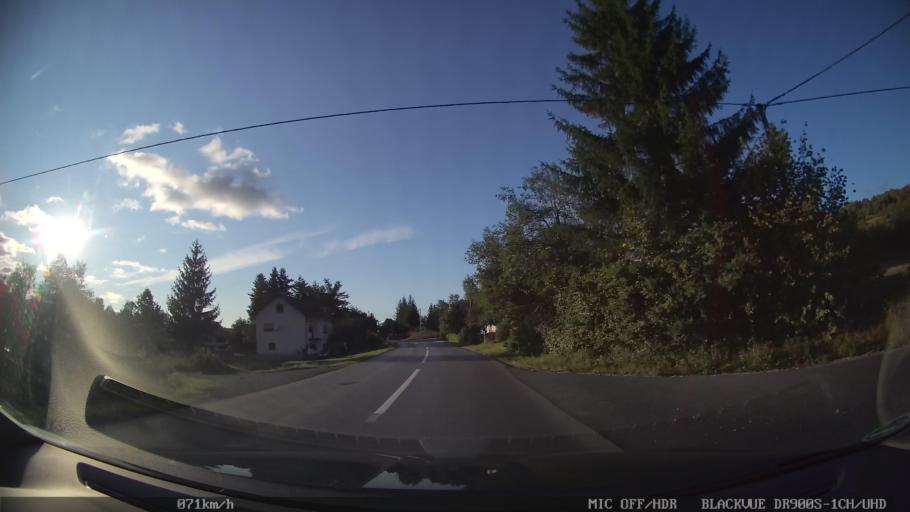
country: HR
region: Karlovacka
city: Plaski
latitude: 45.1477
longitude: 15.3371
